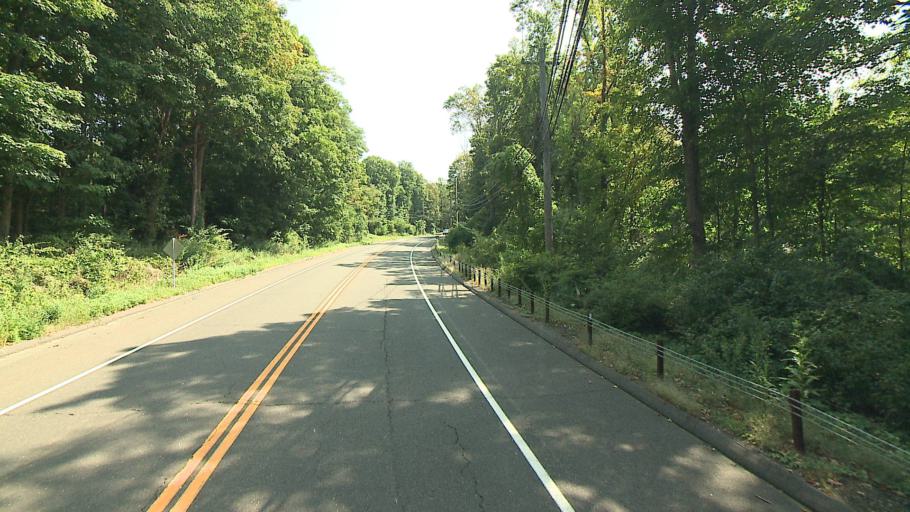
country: US
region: Connecticut
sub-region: Fairfield County
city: Georgetown
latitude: 41.2526
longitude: -73.4201
